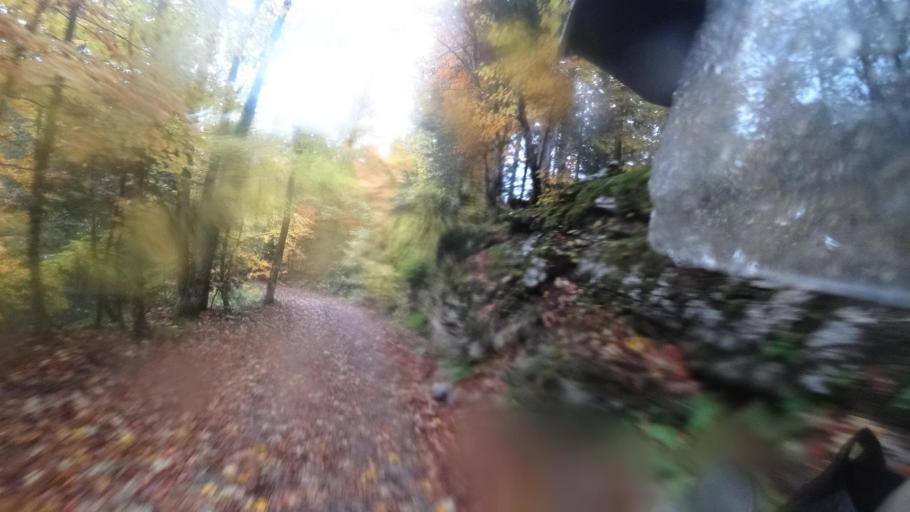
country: HR
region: Primorsko-Goranska
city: Vrbovsko
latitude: 45.3304
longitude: 15.0685
